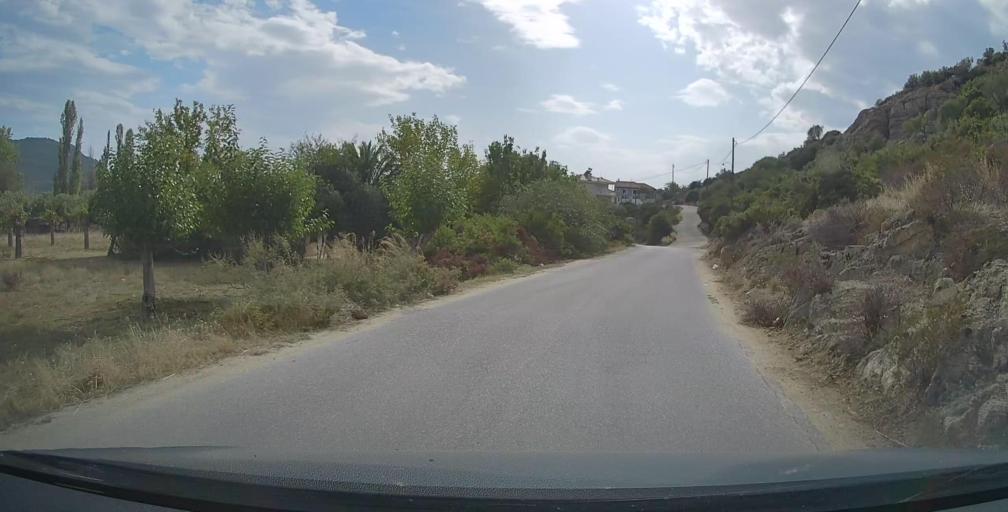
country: GR
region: Central Macedonia
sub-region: Nomos Chalkidikis
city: Sykia
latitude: 39.9884
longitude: 23.9091
